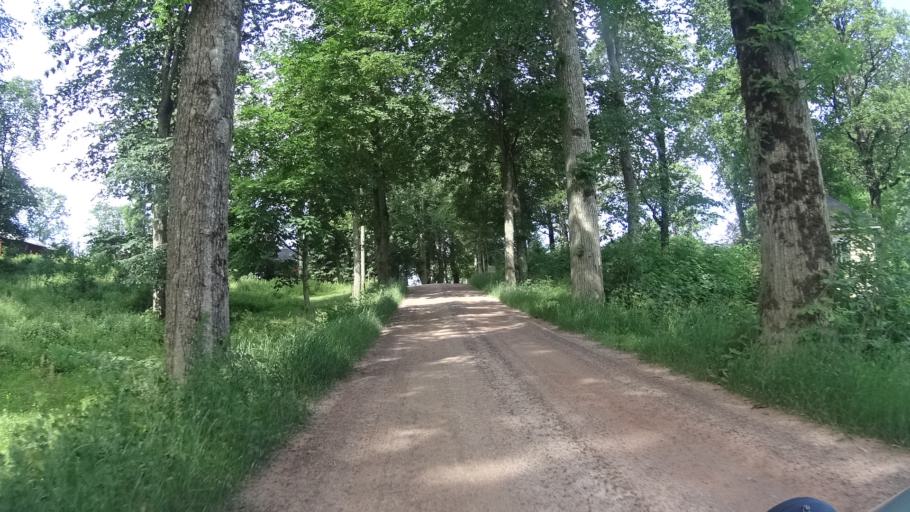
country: SE
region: Kalmar
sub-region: Vasterviks Kommun
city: Overum
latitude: 57.8716
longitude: 16.1723
